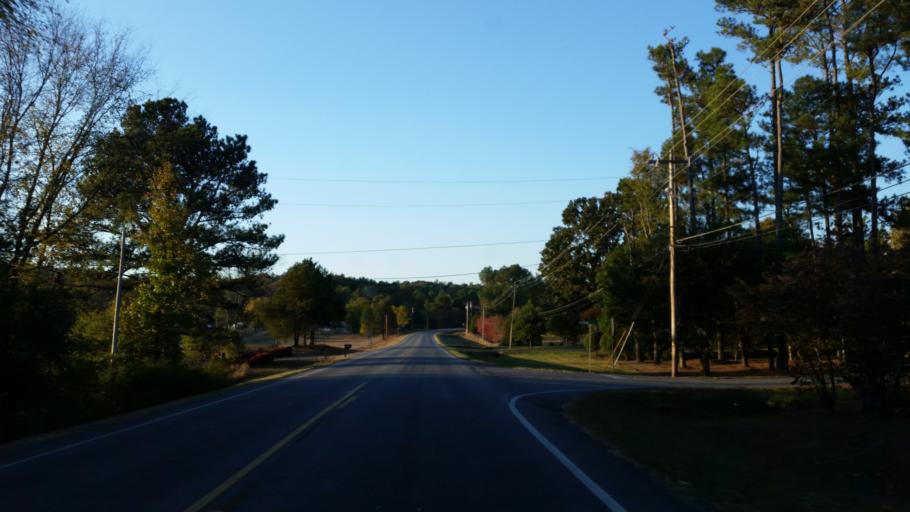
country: US
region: Georgia
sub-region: Gordon County
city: Calhoun
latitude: 34.5240
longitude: -84.9703
